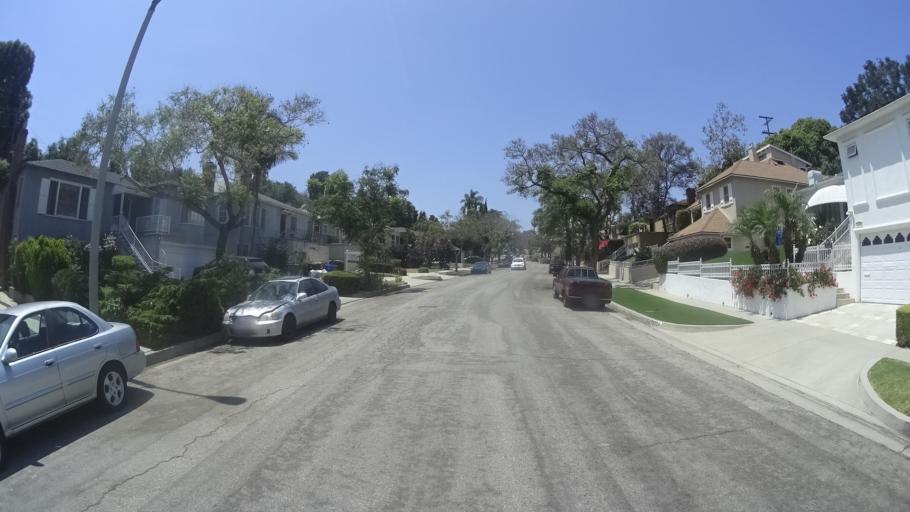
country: US
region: California
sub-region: Los Angeles County
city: View Park-Windsor Hills
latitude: 33.9934
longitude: -118.3510
